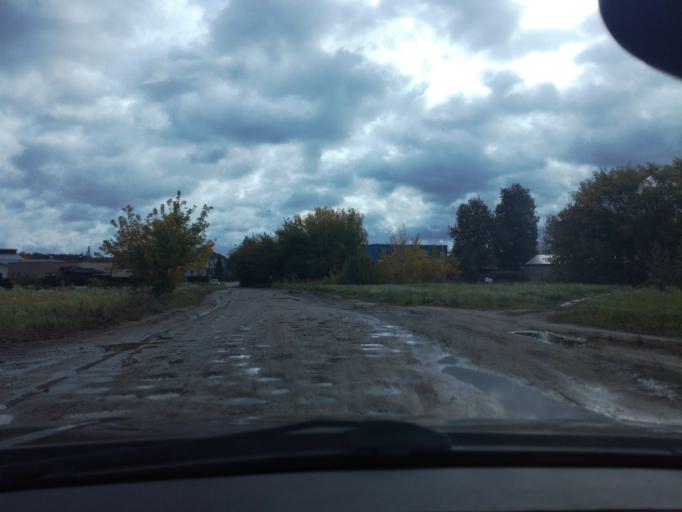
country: LT
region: Alytaus apskritis
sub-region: Alytus
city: Alytus
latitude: 54.3882
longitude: 24.0495
